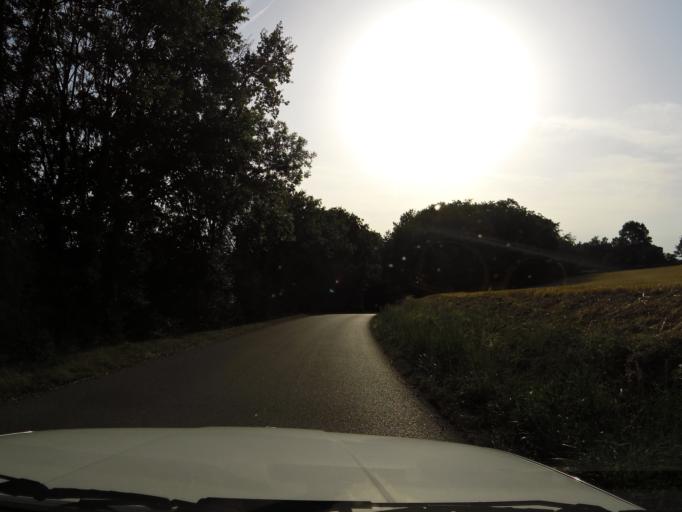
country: FR
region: Rhone-Alpes
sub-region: Departement de l'Ain
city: Perouges
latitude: 45.9303
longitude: 5.1674
